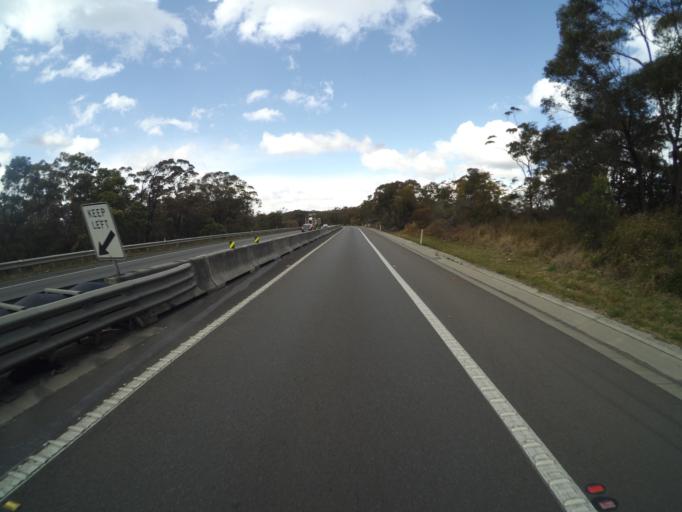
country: AU
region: New South Wales
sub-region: Wollongong
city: Mount Keira
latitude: -34.3448
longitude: 150.7968
